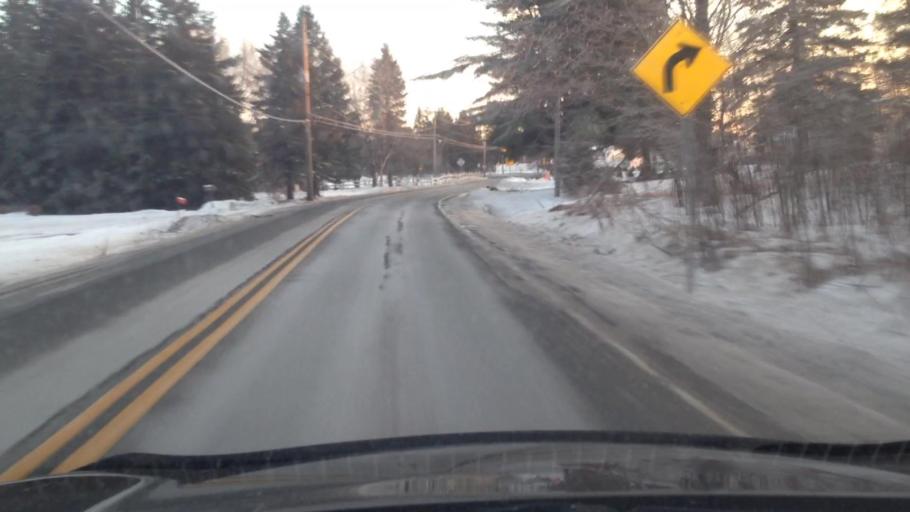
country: CA
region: Quebec
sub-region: Lanaudiere
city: Sainte-Julienne
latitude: 45.9176
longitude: -73.7386
